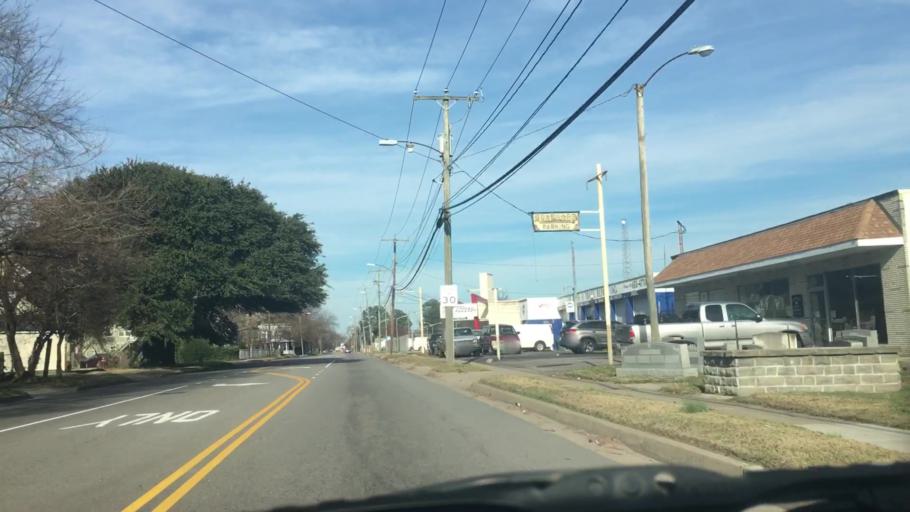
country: US
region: Virginia
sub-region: City of Norfolk
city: Norfolk
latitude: 36.8785
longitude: -76.2530
